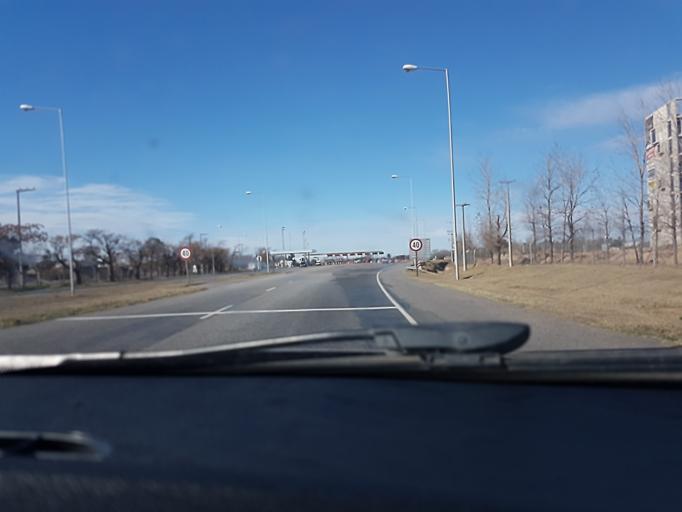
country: AR
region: Cordoba
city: Villa Allende
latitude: -31.3098
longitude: -64.2201
